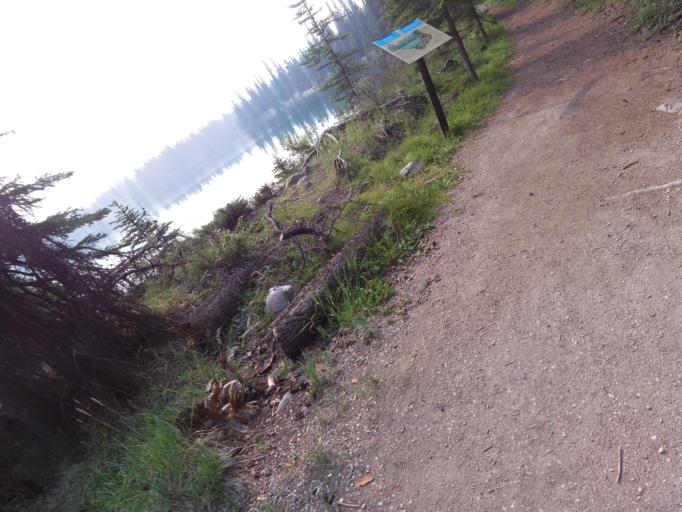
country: CA
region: Alberta
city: Jasper Park Lodge
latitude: 52.8813
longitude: -118.0651
